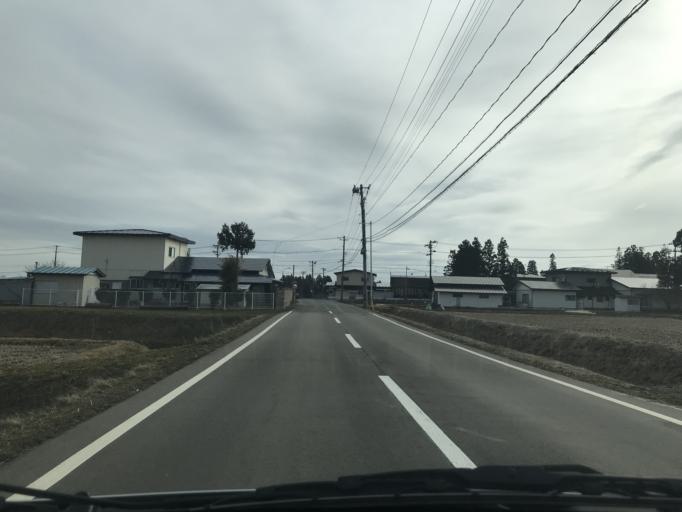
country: JP
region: Iwate
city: Hanamaki
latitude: 39.3998
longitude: 141.0752
